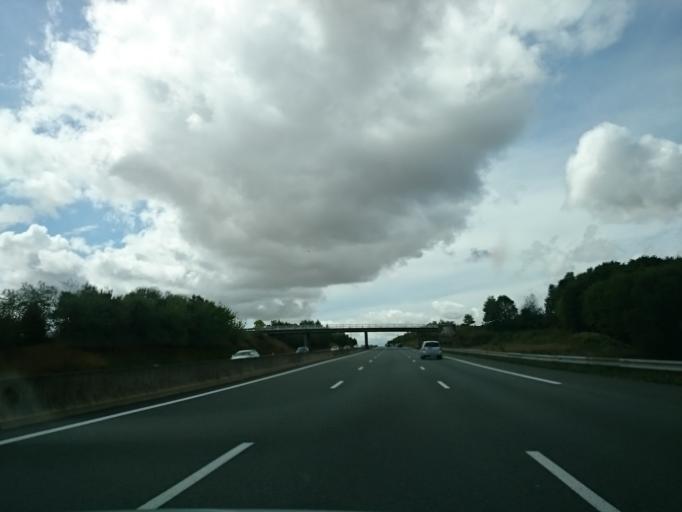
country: FR
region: Centre
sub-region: Departement d'Eure-et-Loir
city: Brou
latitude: 48.2656
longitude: 1.1481
